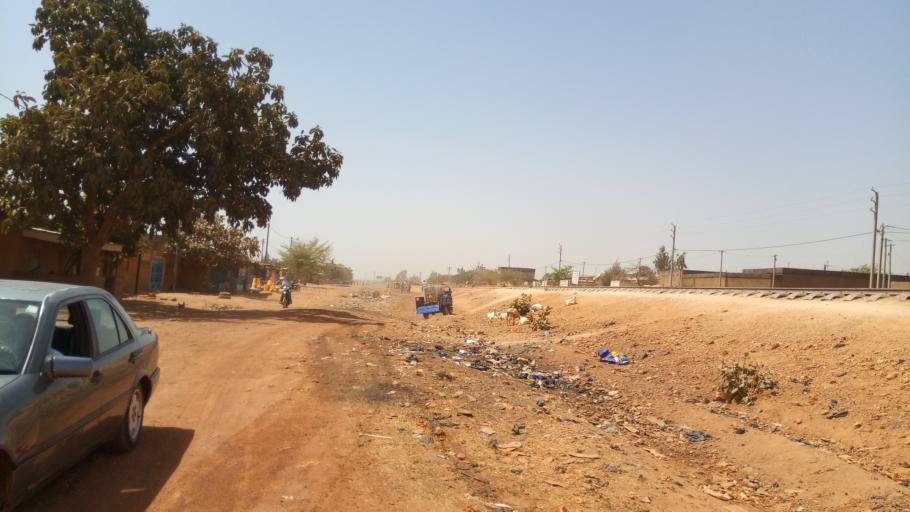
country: BF
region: Centre
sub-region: Kadiogo Province
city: Ouagadougou
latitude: 12.3855
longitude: -1.5658
